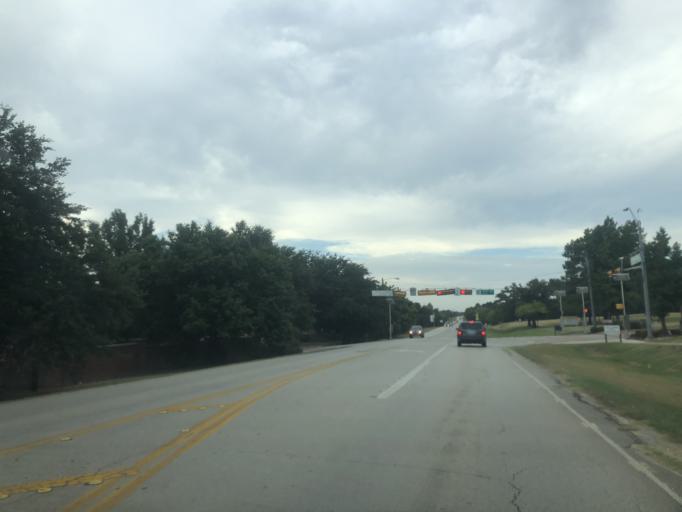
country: US
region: Texas
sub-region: Tarrant County
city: Southlake
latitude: 32.9530
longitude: -97.1511
